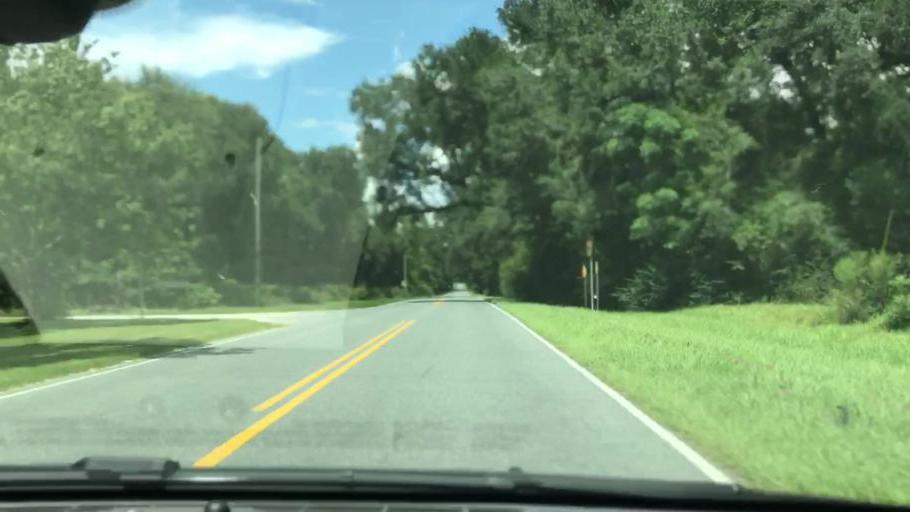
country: US
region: Florida
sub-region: Jackson County
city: Malone
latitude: 30.9401
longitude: -85.1183
